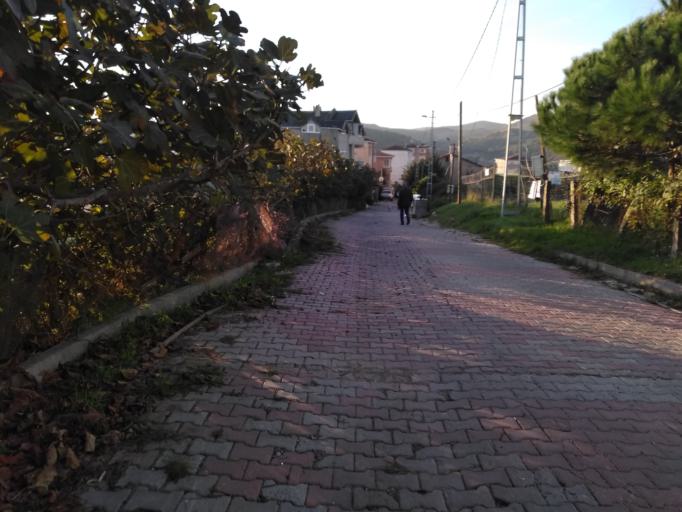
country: TR
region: Istanbul
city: Arikoey
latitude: 41.2388
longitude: 28.9830
